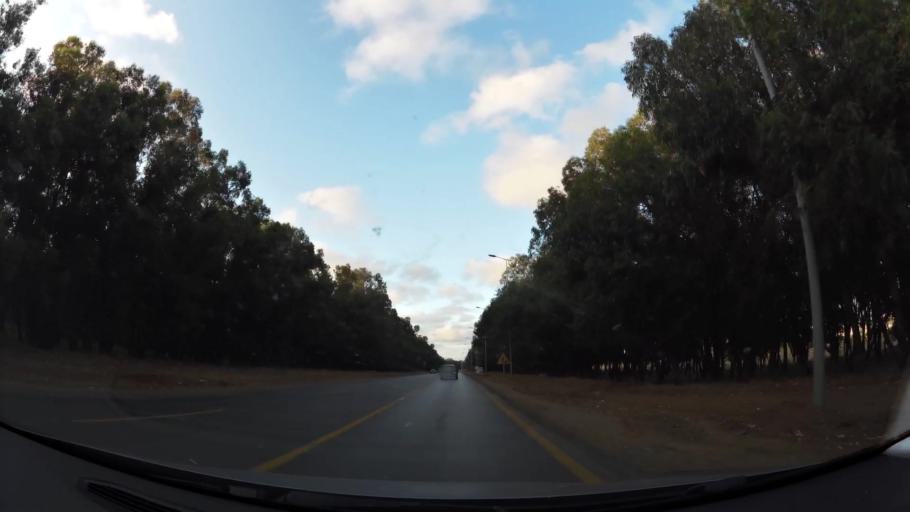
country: MA
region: Gharb-Chrarda-Beni Hssen
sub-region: Kenitra Province
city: Kenitra
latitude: 34.2413
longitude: -6.6254
